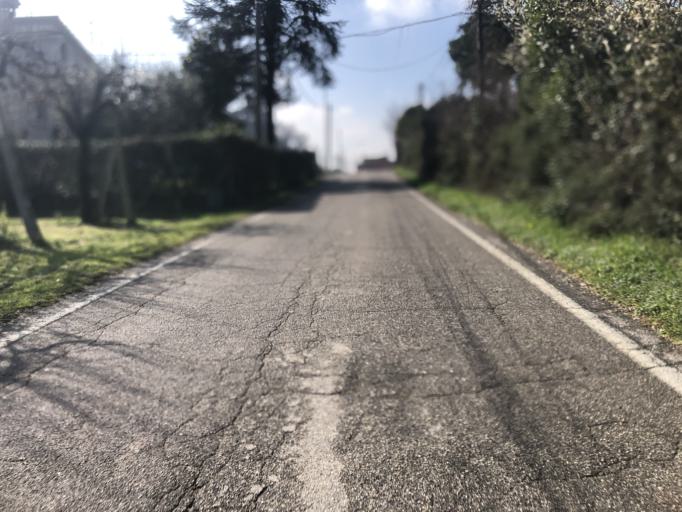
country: IT
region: Veneto
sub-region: Provincia di Verona
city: Rosegaferro
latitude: 45.3844
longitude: 10.7957
